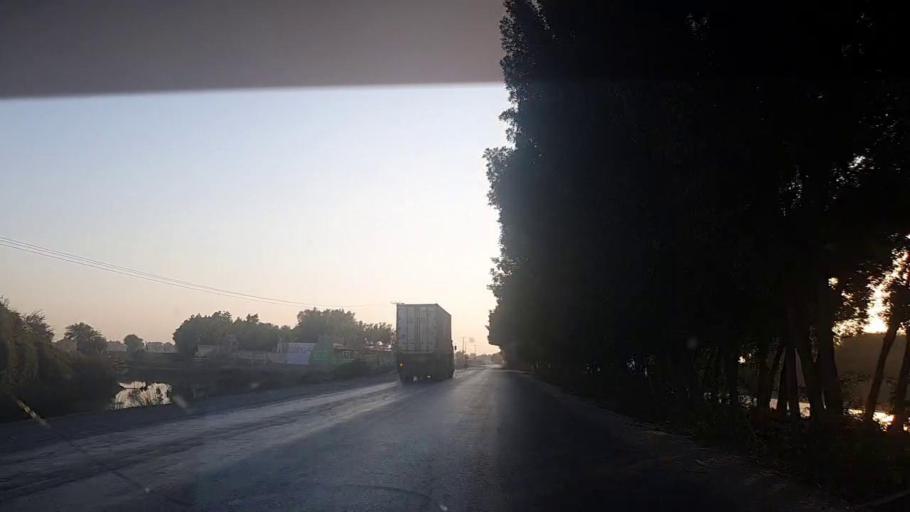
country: PK
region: Sindh
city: Hingorja
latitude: 27.1844
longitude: 68.4022
